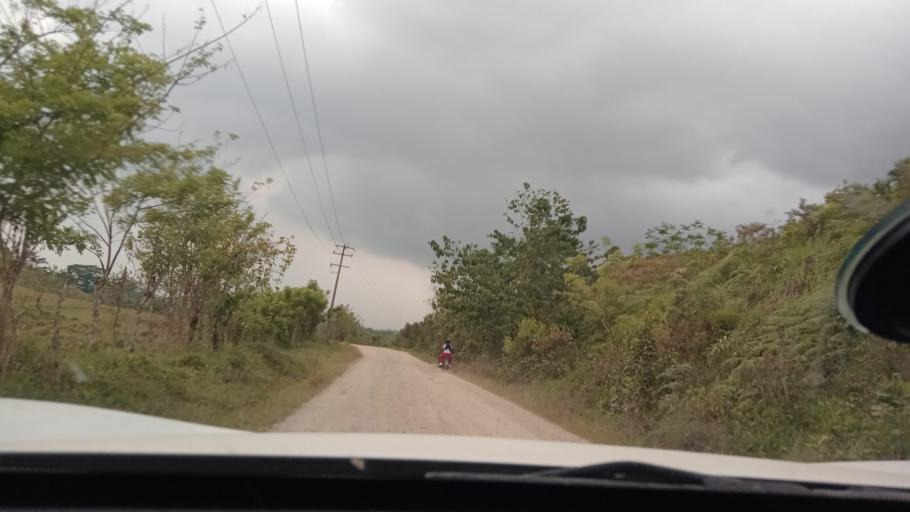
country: MX
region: Tabasco
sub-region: Huimanguillo
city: Francisco Rueda
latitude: 17.4353
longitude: -94.0533
